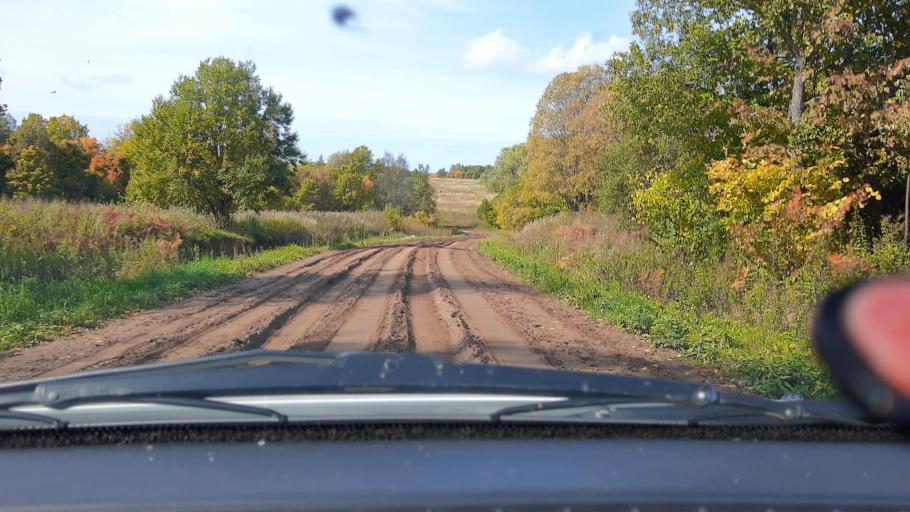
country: RU
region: Bashkortostan
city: Kudeyevskiy
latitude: 54.7150
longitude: 56.6343
